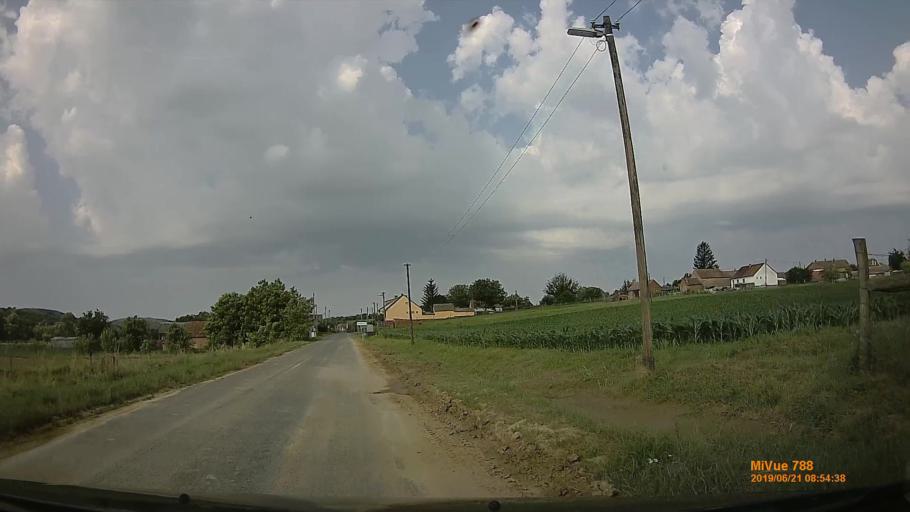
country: HU
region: Baranya
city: Buekkoesd
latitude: 46.1637
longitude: 17.8840
